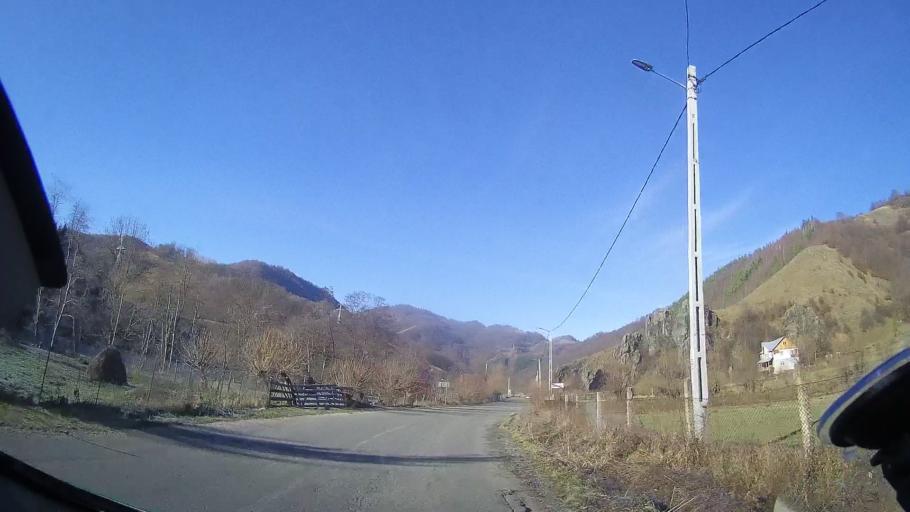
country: RO
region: Cluj
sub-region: Comuna Sacueu
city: Sacuieu
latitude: 46.8279
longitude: 22.8784
